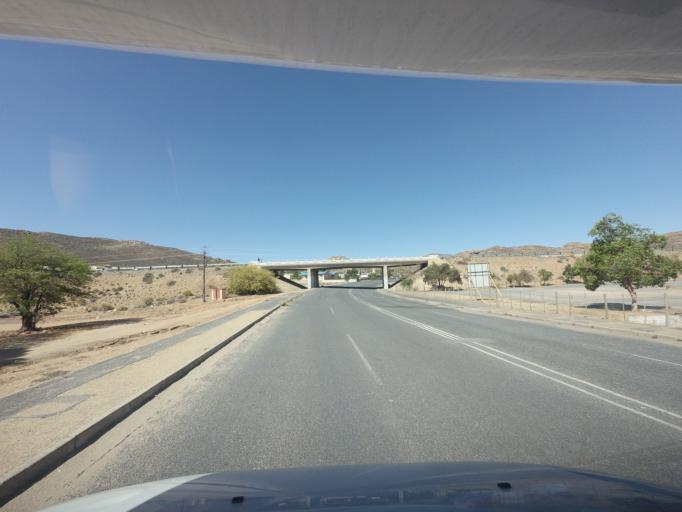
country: ZA
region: Northern Cape
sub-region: Namakwa District Municipality
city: Springbok
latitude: -29.6619
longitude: 17.8920
